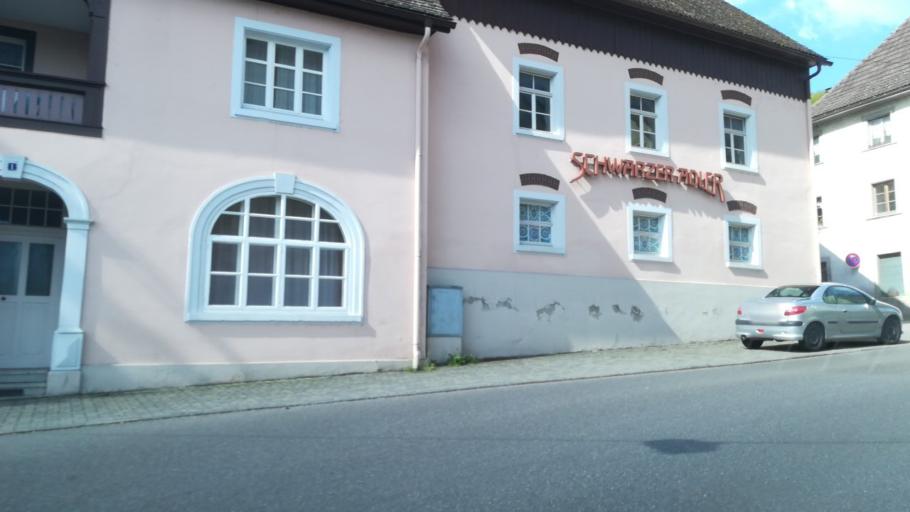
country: DE
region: Baden-Wuerttemberg
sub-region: Freiburg Region
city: Stuhlingen
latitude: 47.7413
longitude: 8.4401
